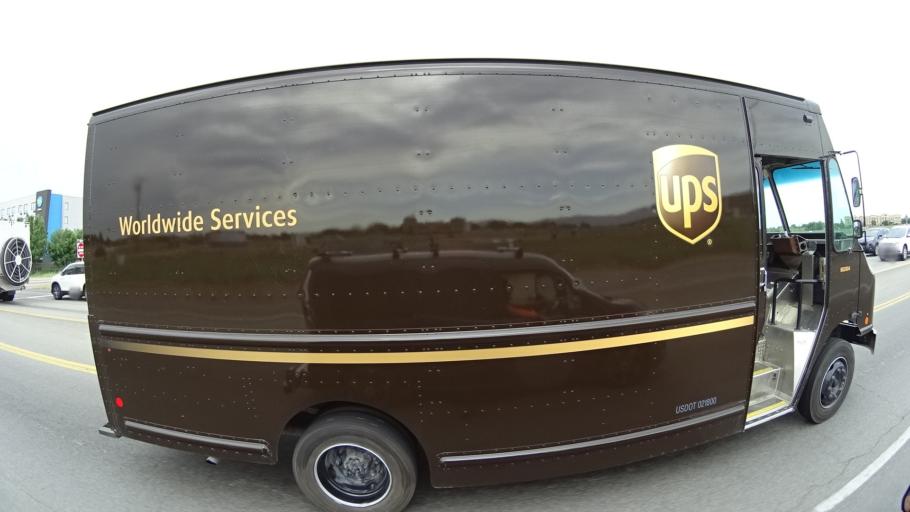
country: US
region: Idaho
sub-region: Ada County
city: Meridian
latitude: 43.5918
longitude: -116.3536
